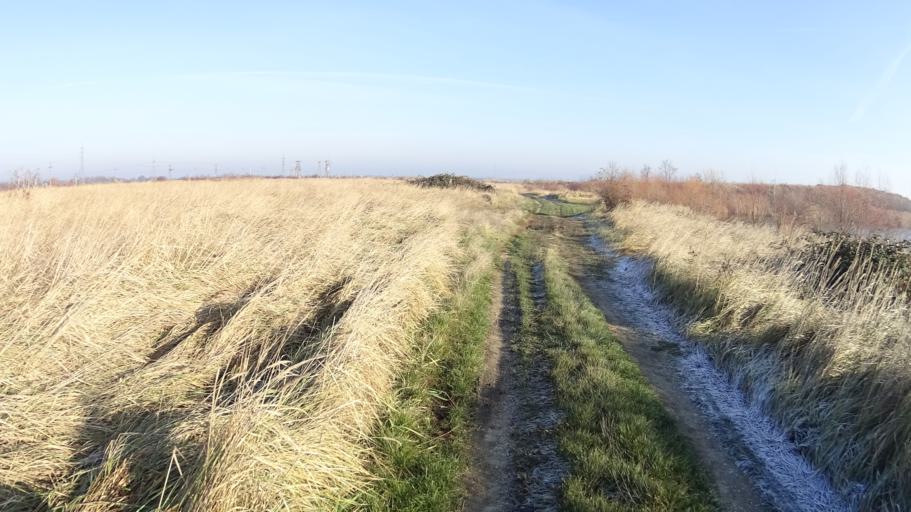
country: HU
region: Borsod-Abauj-Zemplen
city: Onod
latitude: 47.9940
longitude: 20.8756
